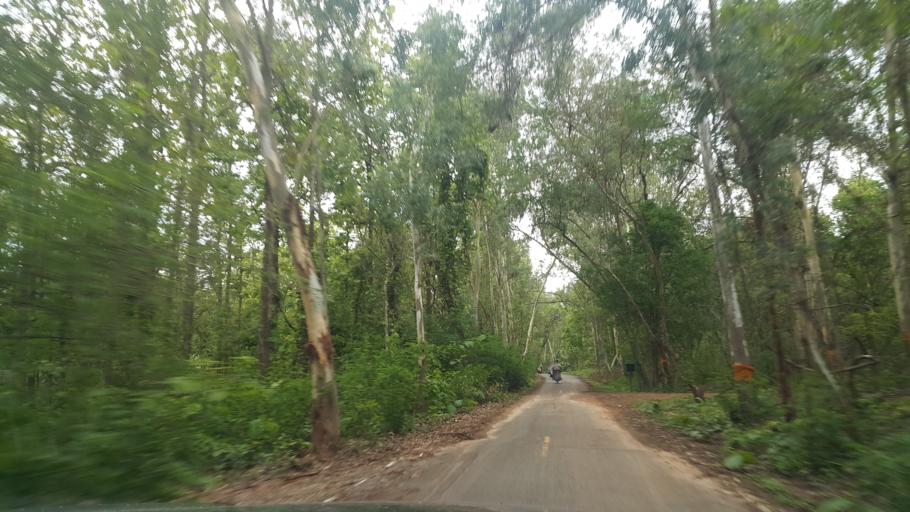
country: TH
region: Chiang Mai
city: Mae On
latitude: 18.7200
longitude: 99.2331
